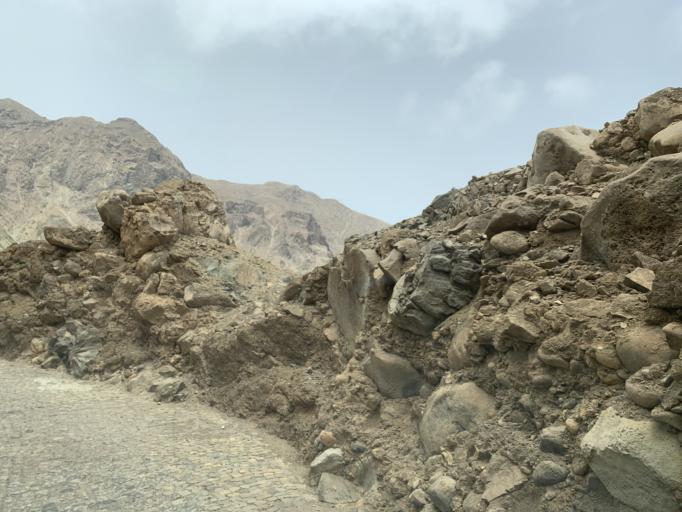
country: CV
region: Brava
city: Vila Nova Sintra
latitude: 14.8760
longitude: -24.7331
